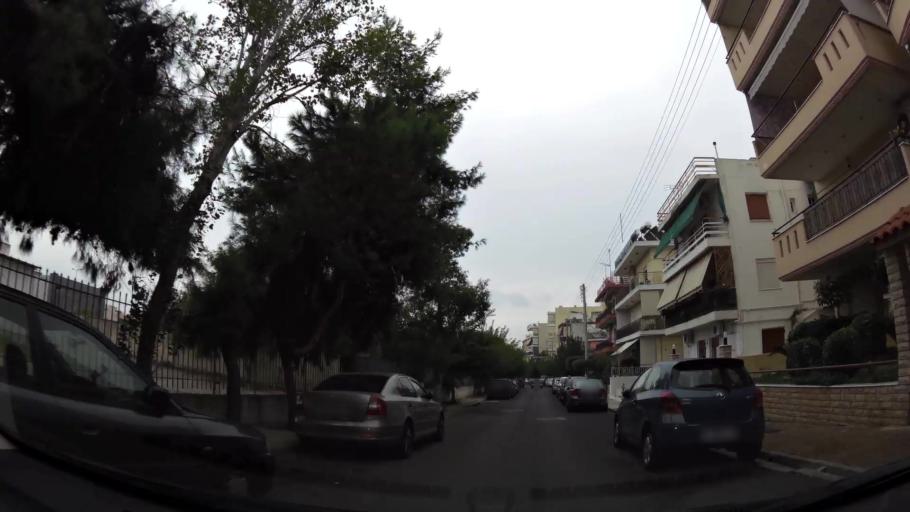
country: GR
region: Attica
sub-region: Nomarchia Athinas
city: Chaidari
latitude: 38.0116
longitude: 23.6568
